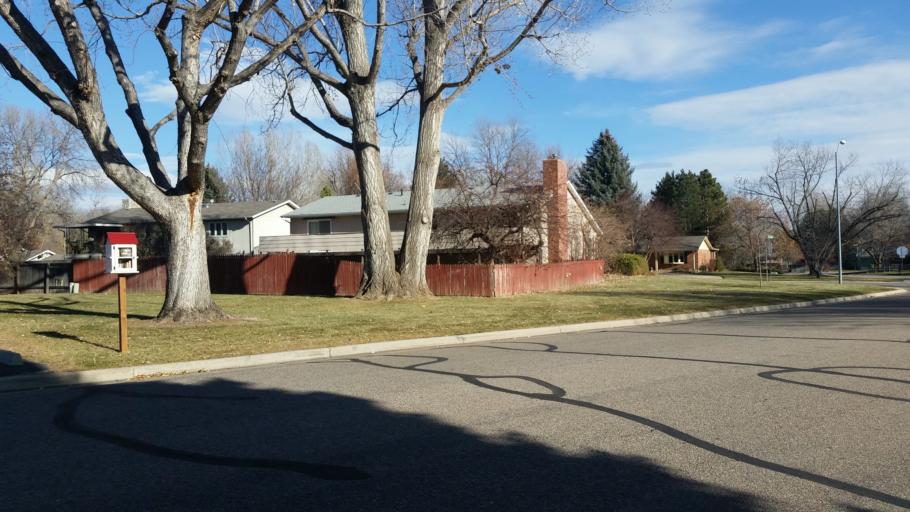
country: US
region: Colorado
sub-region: Larimer County
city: Fort Collins
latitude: 40.5579
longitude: -105.0528
